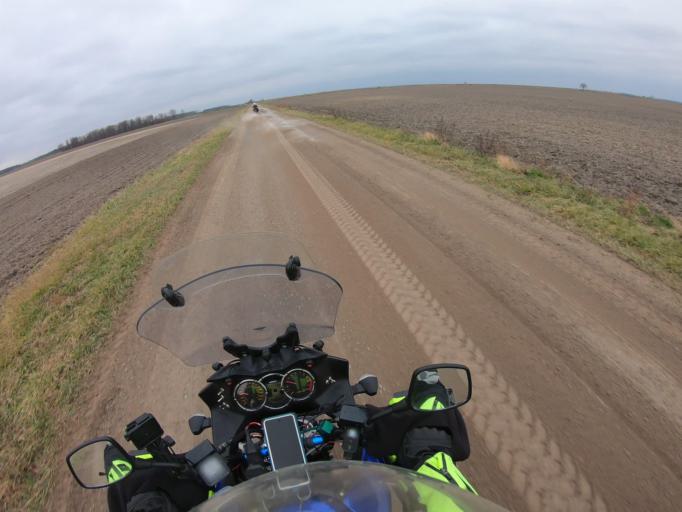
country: US
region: Michigan
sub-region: Saginaw County
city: Burt
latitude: 43.2635
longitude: -83.9817
